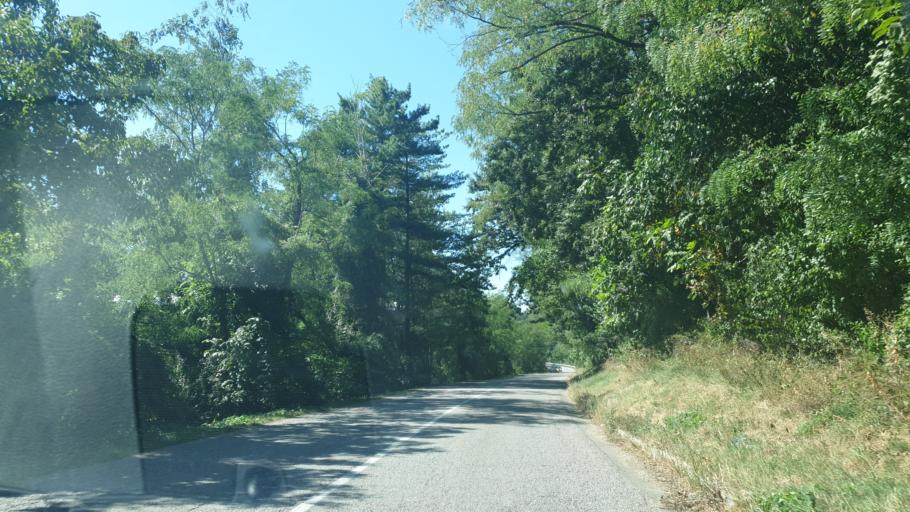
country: RS
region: Central Serbia
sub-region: Kolubarski Okrug
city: Mionica
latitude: 44.2150
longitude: 20.0845
